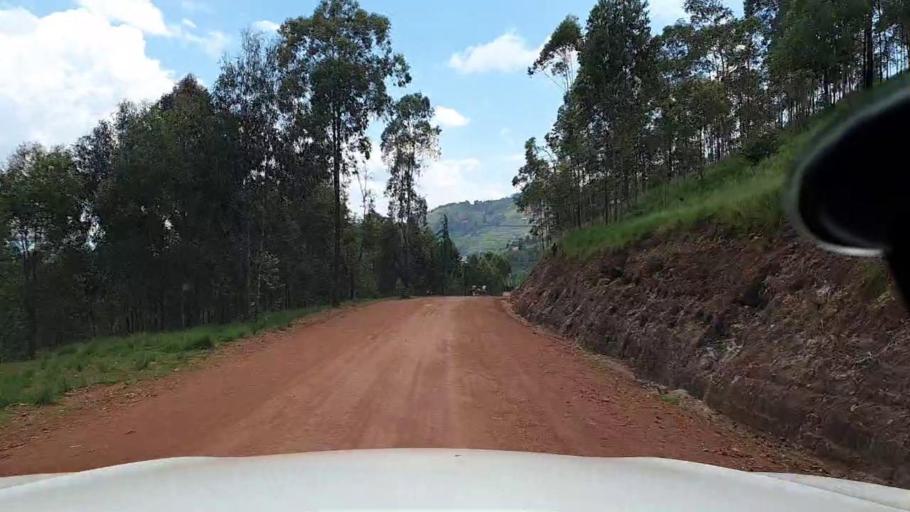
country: RW
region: Kigali
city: Kigali
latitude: -1.7673
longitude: 29.8417
